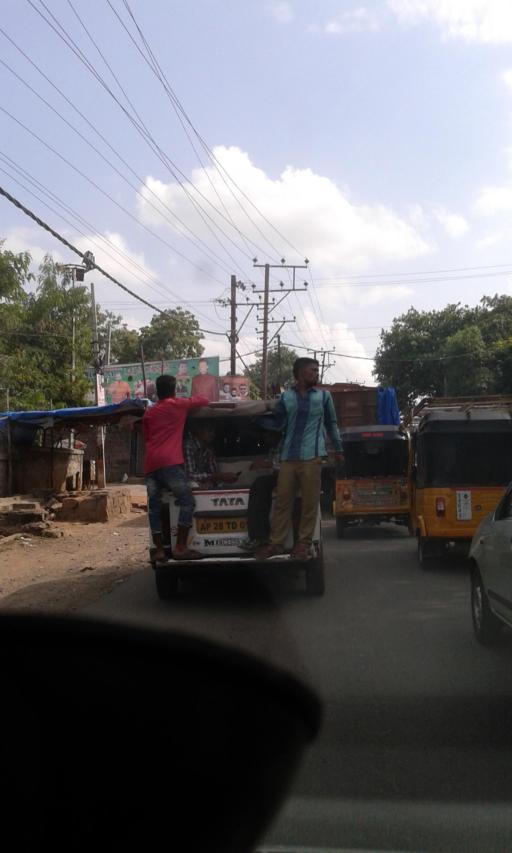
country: IN
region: Telangana
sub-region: Rangareddi
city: Balapur
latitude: 17.3174
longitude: 78.4796
